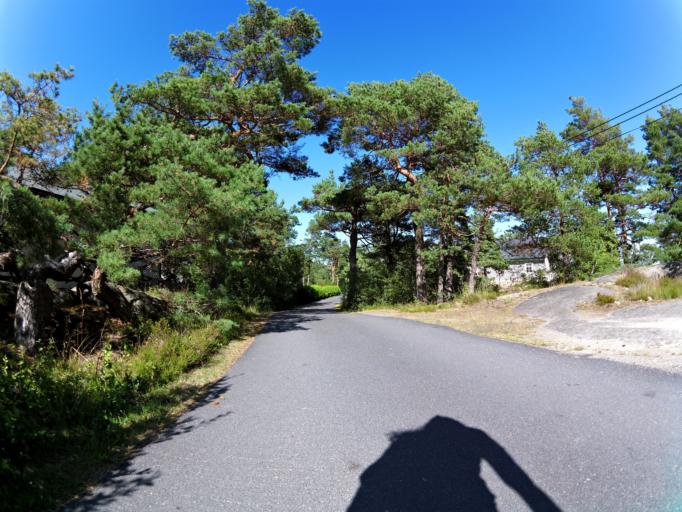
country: NO
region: Ostfold
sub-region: Fredrikstad
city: Fredrikstad
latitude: 59.1666
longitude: 10.8399
